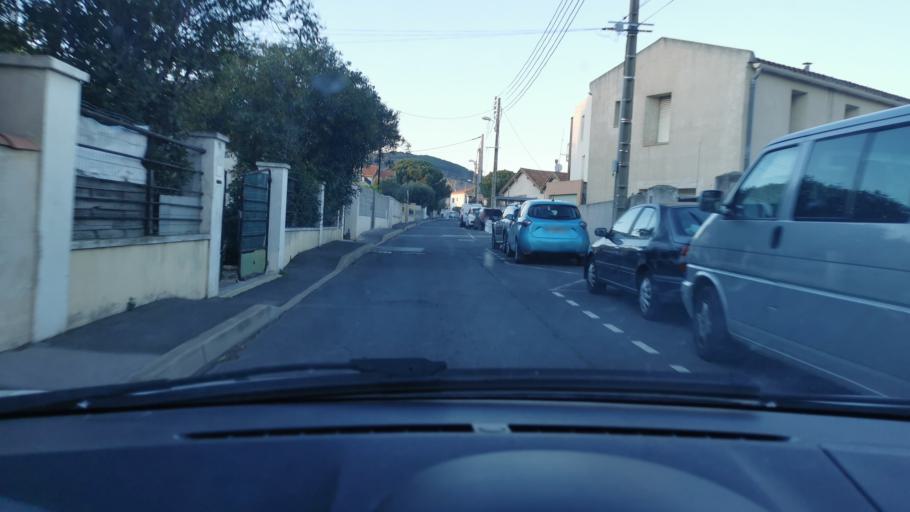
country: FR
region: Languedoc-Roussillon
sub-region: Departement de l'Herault
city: Frontignan
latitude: 43.4515
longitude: 3.7566
